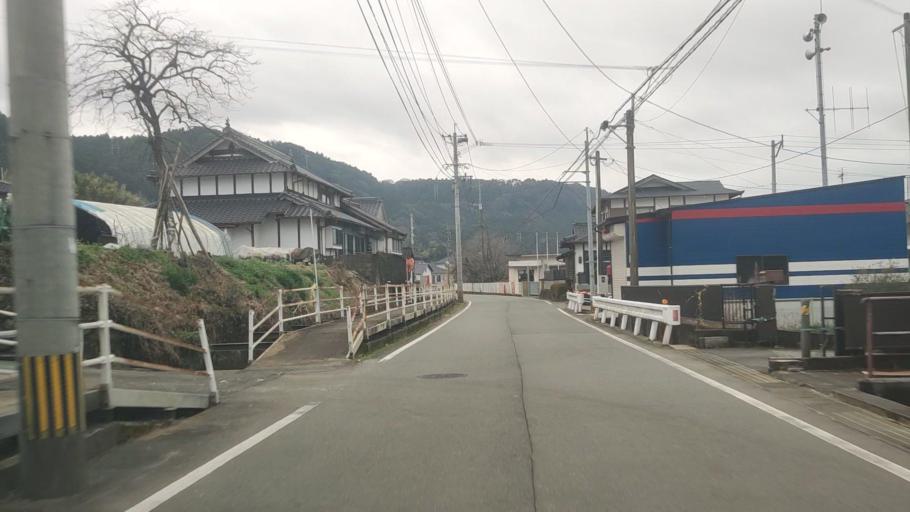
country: JP
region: Kumamoto
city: Ozu
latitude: 32.8559
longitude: 130.8837
